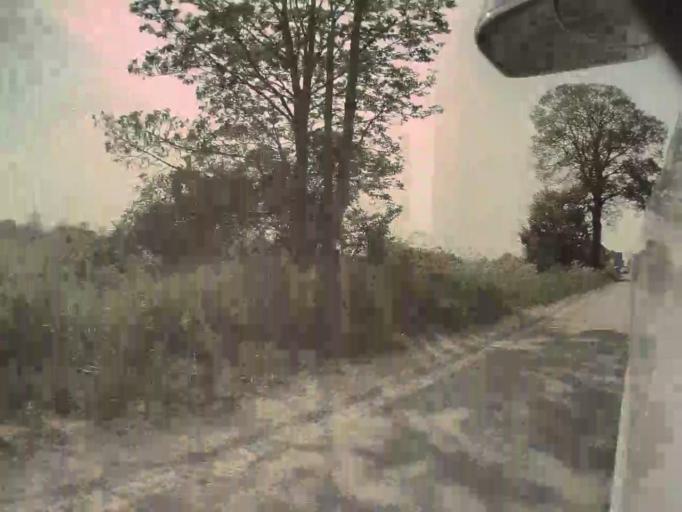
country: BE
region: Wallonia
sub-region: Province de Namur
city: Dinant
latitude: 50.2644
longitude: 4.9543
